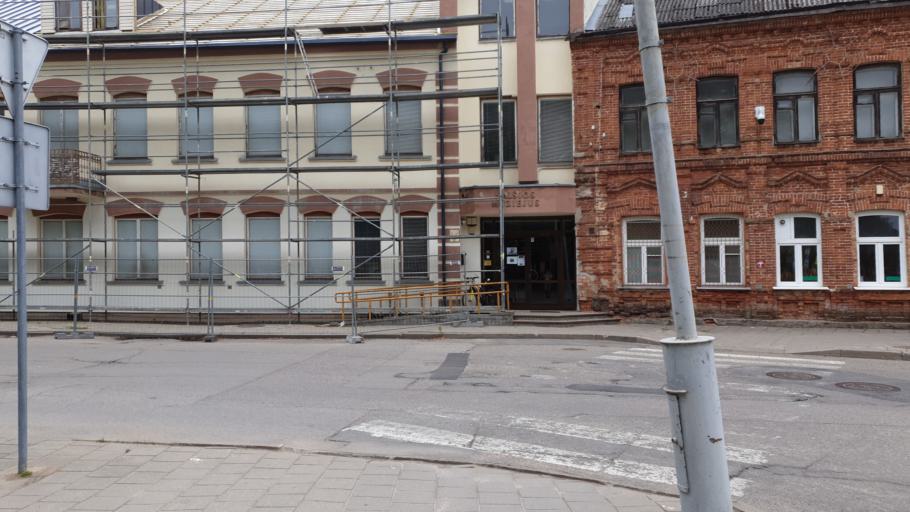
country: LT
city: Svencionys
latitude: 55.1347
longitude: 26.1597
